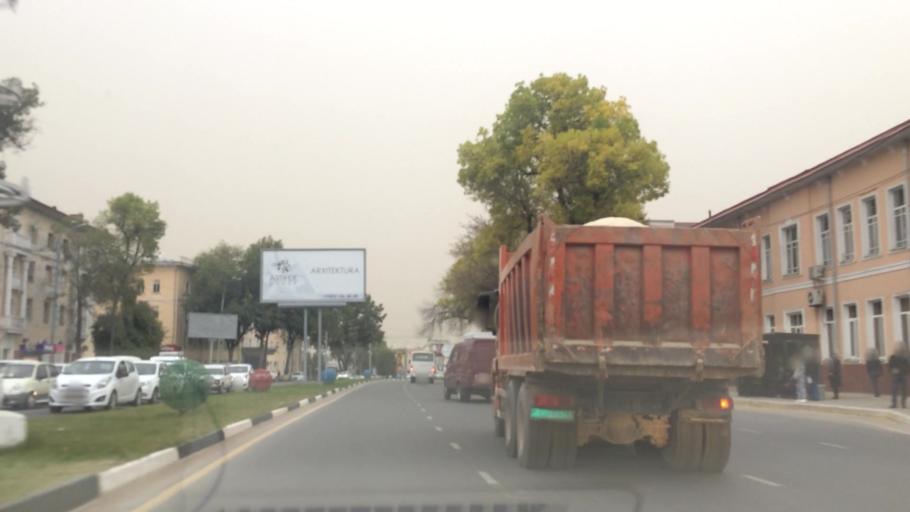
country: UZ
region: Toshkent Shahri
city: Tashkent
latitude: 41.3041
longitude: 69.2474
